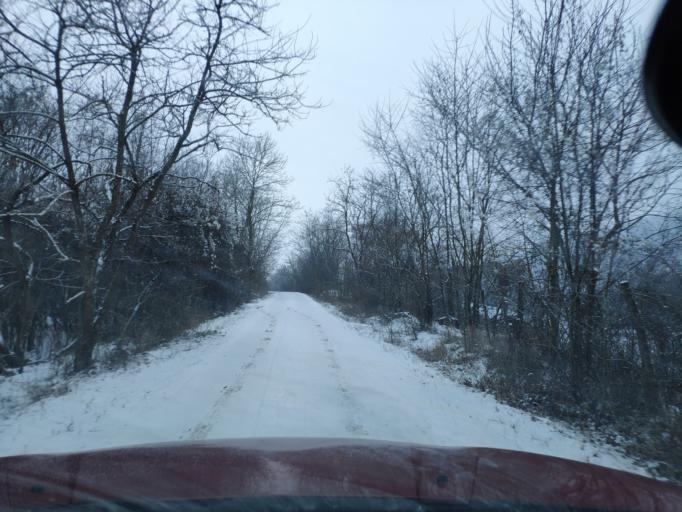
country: SK
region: Nitriansky
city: Sahy
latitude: 48.1690
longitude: 19.0148
